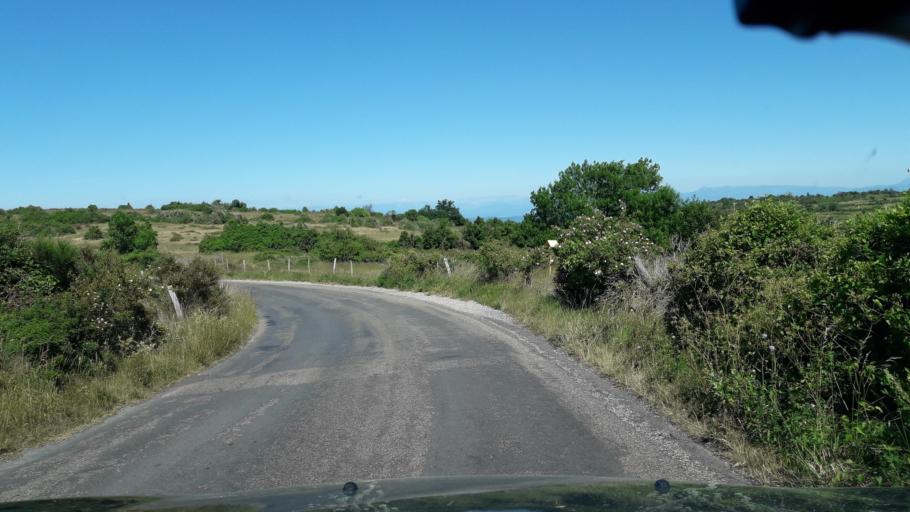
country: FR
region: Rhone-Alpes
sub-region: Departement de l'Ardeche
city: Saint-Priest
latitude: 44.6925
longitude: 4.5764
